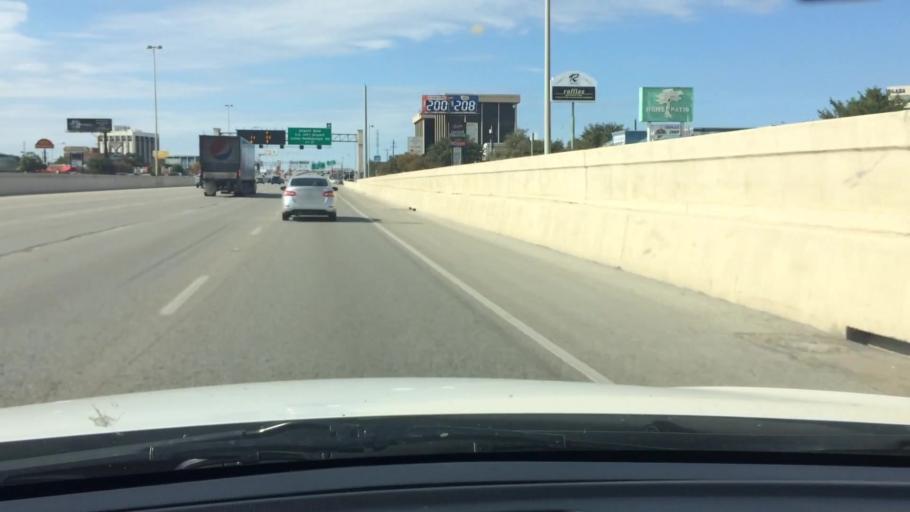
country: US
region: Texas
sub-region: Bexar County
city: Alamo Heights
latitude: 29.5168
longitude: -98.4557
